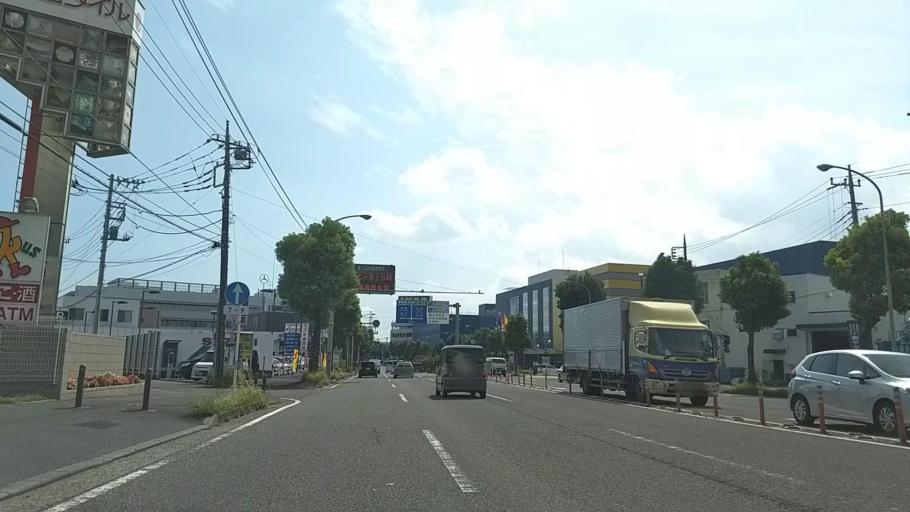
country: JP
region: Kanagawa
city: Yokohama
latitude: 35.5242
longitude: 139.5919
